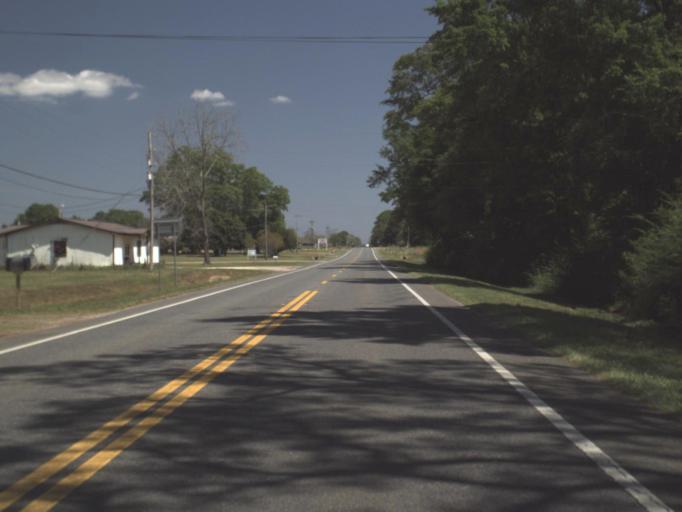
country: US
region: Florida
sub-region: Escambia County
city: Century
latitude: 30.9527
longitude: -87.1412
